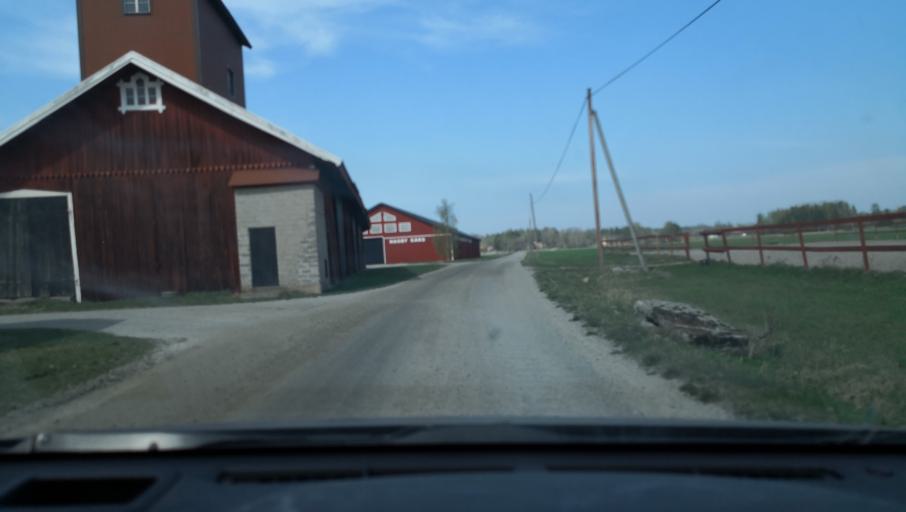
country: SE
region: Vaestmanland
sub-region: Vasteras
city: Skultuna
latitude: 59.7966
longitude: 16.4372
